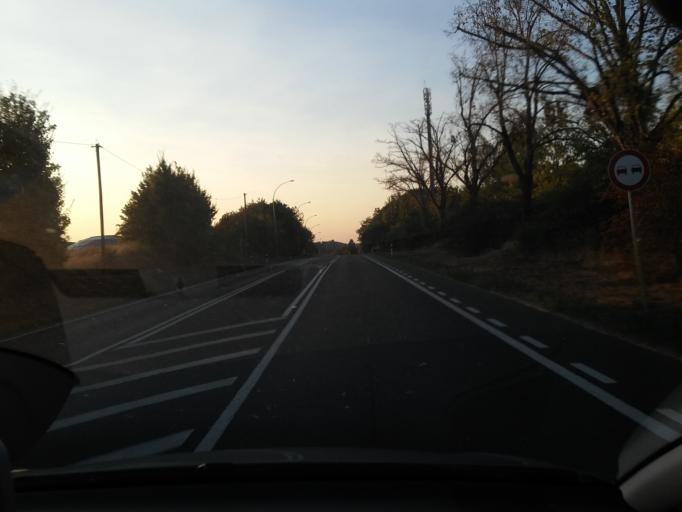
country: LU
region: Luxembourg
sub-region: Canton de Luxembourg
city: Alzingen
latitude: 49.5581
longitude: 6.1682
